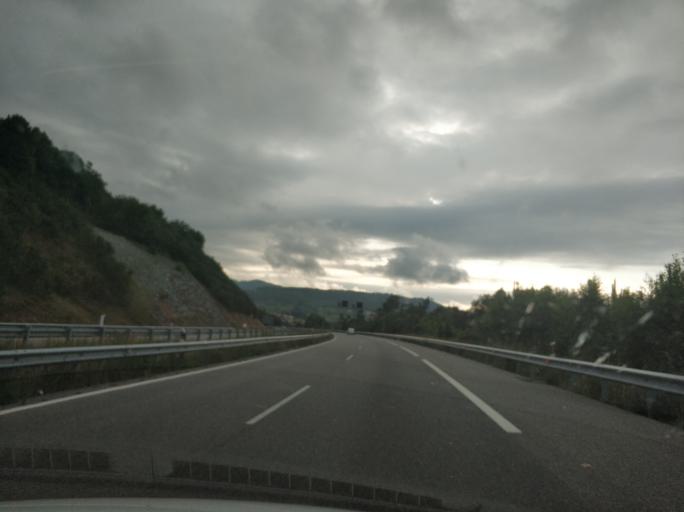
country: ES
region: Asturias
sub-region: Province of Asturias
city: Cudillero
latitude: 43.5445
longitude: -6.1365
